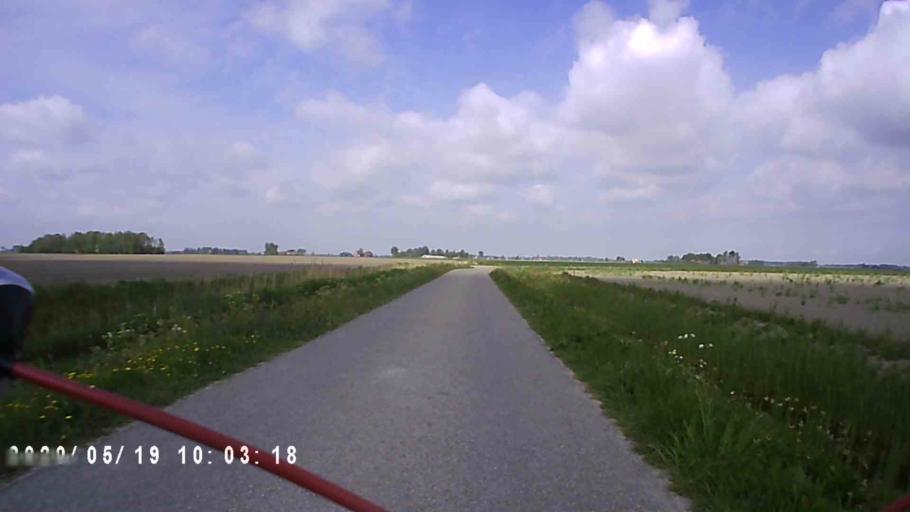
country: NL
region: Friesland
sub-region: Gemeente Kollumerland en Nieuwkruisland
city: Kollum
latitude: 53.3020
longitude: 6.2298
